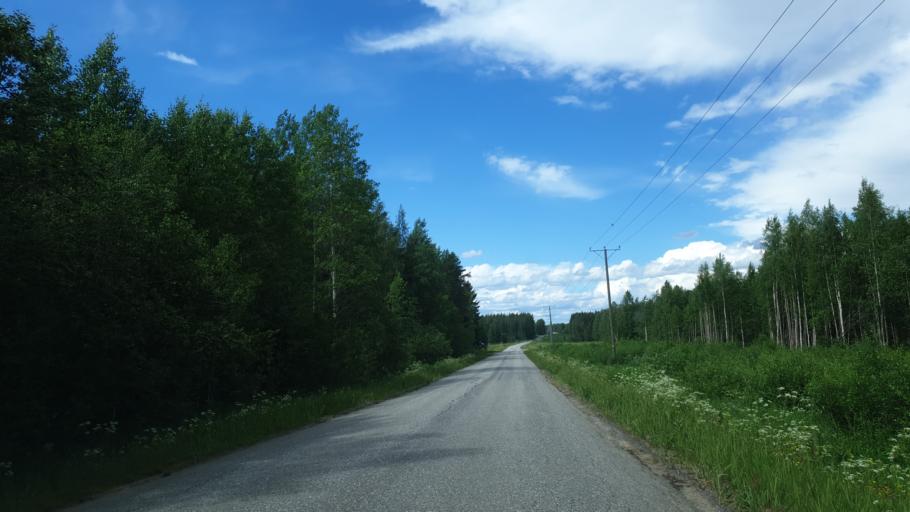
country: FI
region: Northern Savo
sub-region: Koillis-Savo
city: Kaavi
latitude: 62.9827
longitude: 28.7407
